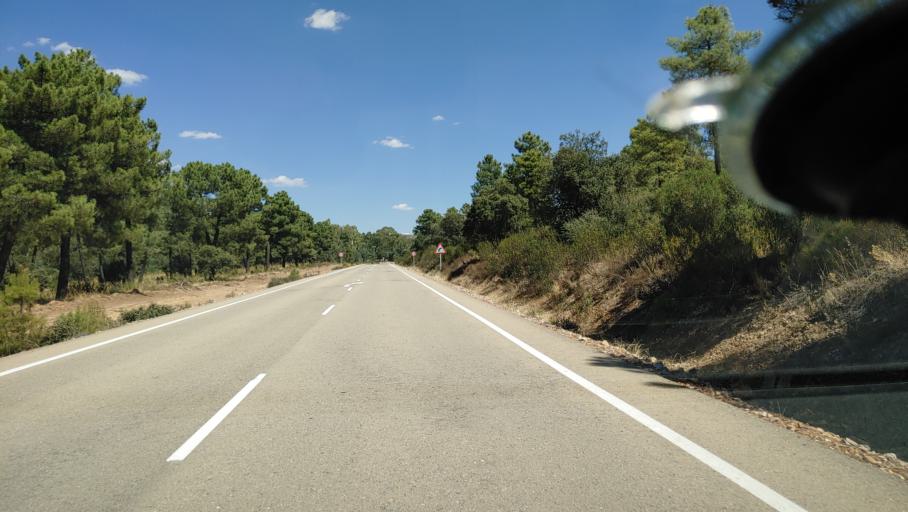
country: ES
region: Castille-La Mancha
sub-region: Provincia de Ciudad Real
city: Saceruela
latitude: 38.9898
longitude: -4.5420
